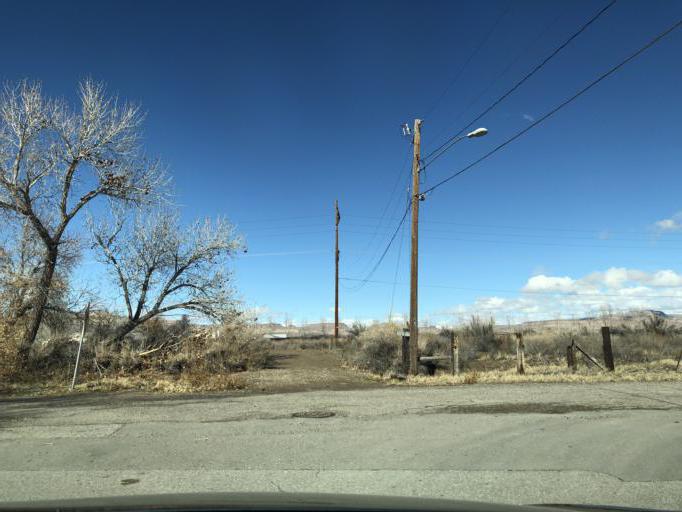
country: US
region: Utah
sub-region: Carbon County
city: East Carbon City
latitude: 39.0001
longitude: -110.1599
